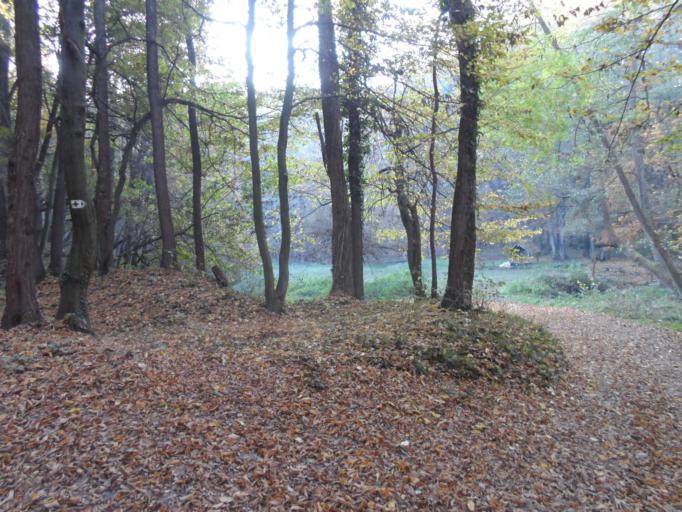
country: HU
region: Veszprem
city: Ajka
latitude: 47.1861
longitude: 17.5952
